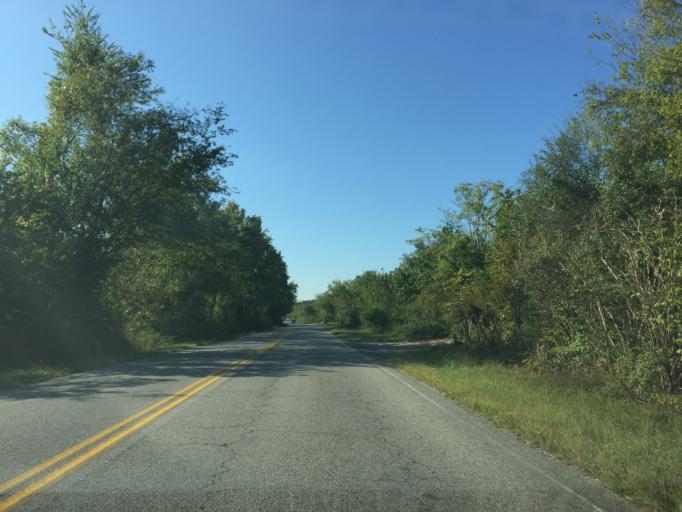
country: US
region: Tennessee
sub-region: Hamilton County
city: Harrison
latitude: 35.0940
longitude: -85.1605
